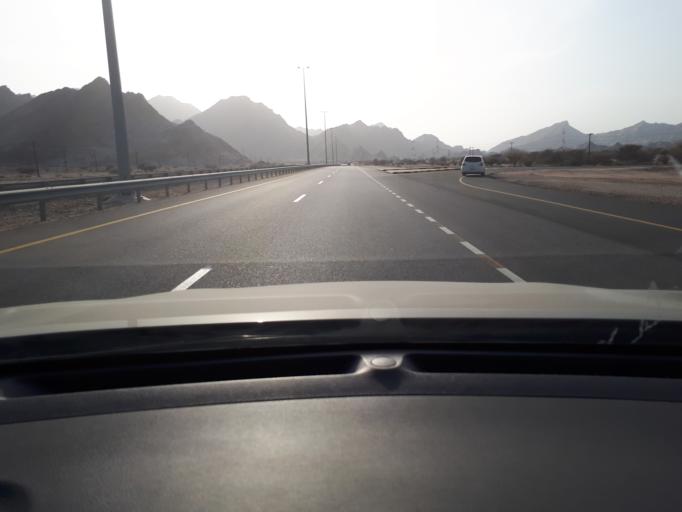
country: OM
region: Muhafazat Masqat
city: Muscat
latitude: 23.3666
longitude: 58.6513
